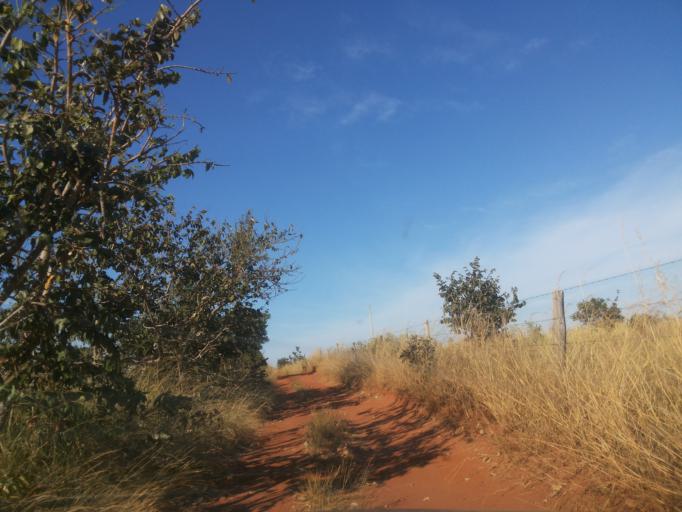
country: BR
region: Minas Gerais
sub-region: Ituiutaba
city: Ituiutaba
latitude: -19.1216
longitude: -49.3959
